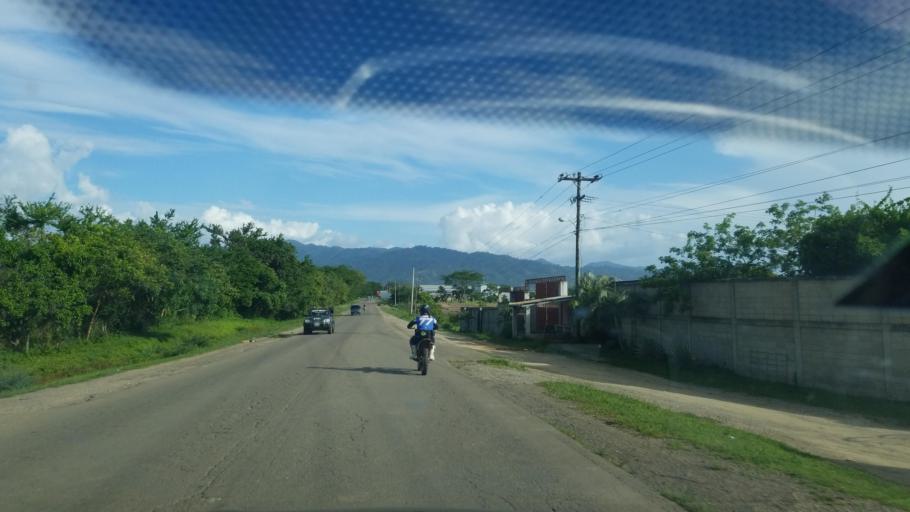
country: HN
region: El Paraiso
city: Cuyali
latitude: 13.9029
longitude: -86.5559
